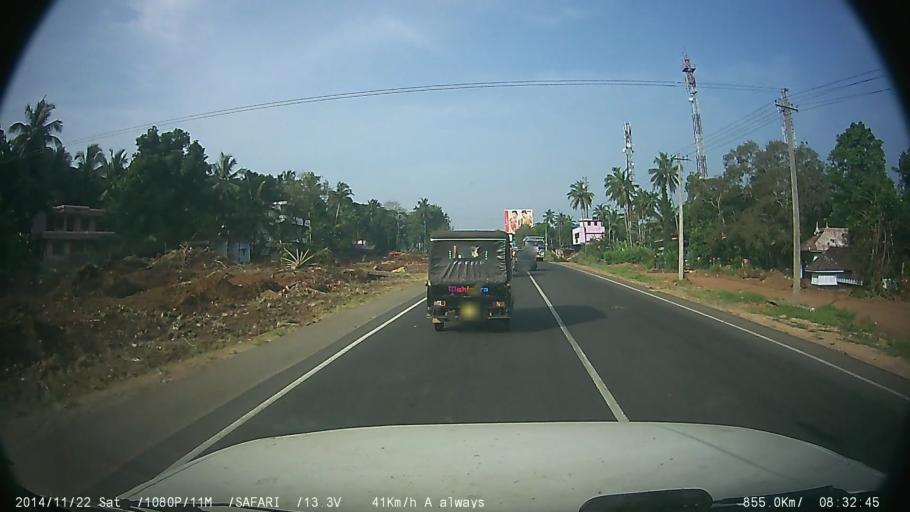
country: IN
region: Kerala
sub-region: Thrissur District
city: Trichur
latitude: 10.5508
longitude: 76.3081
